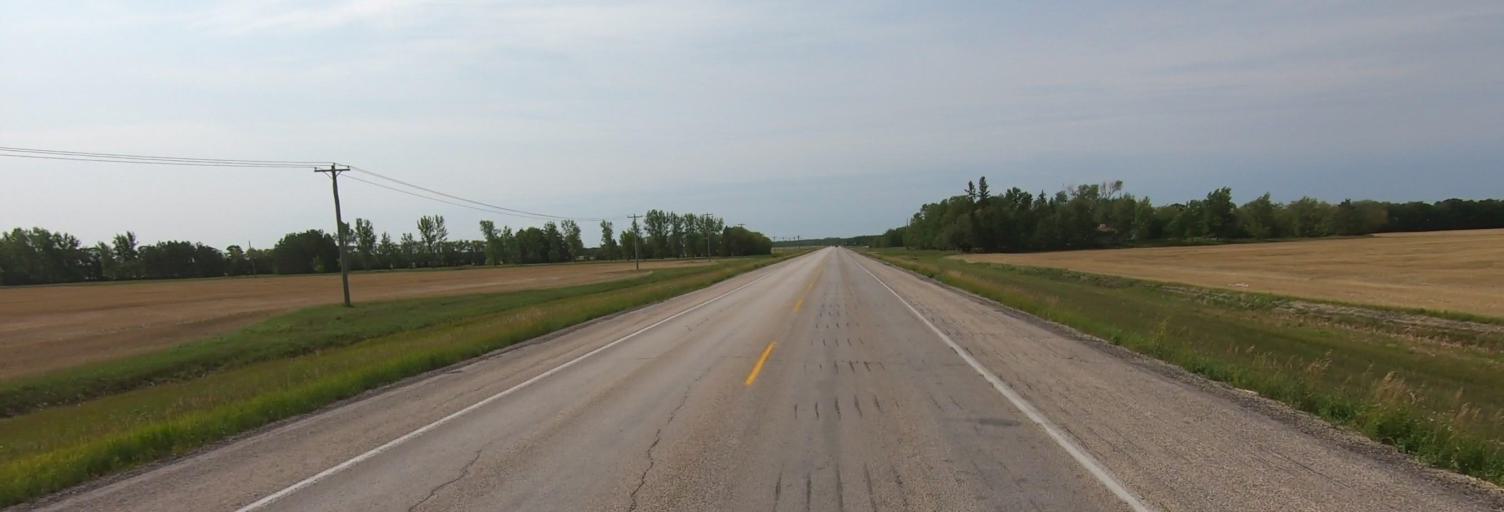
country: CA
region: Manitoba
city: Niverville
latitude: 49.6118
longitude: -97.1248
